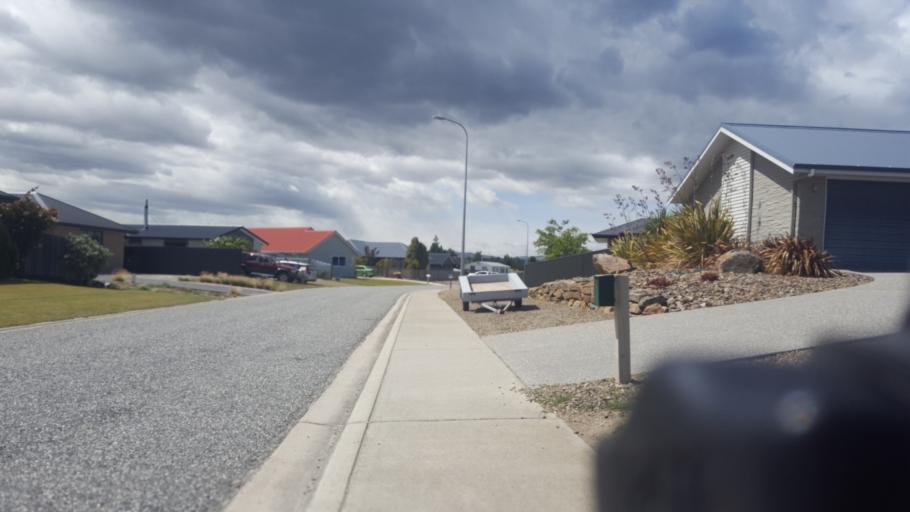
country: NZ
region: Otago
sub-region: Queenstown-Lakes District
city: Wanaka
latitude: -45.1953
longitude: 169.3336
